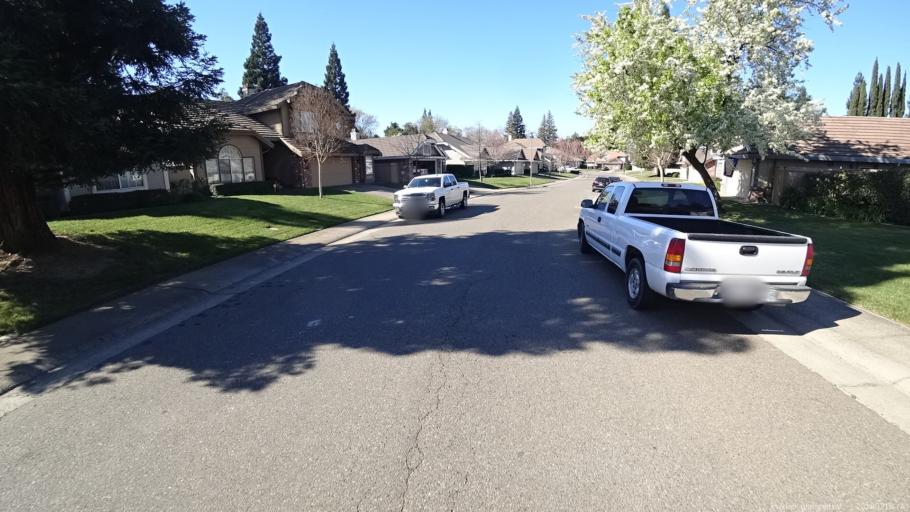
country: US
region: California
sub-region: Sacramento County
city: Gold River
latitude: 38.6207
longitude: -121.2565
